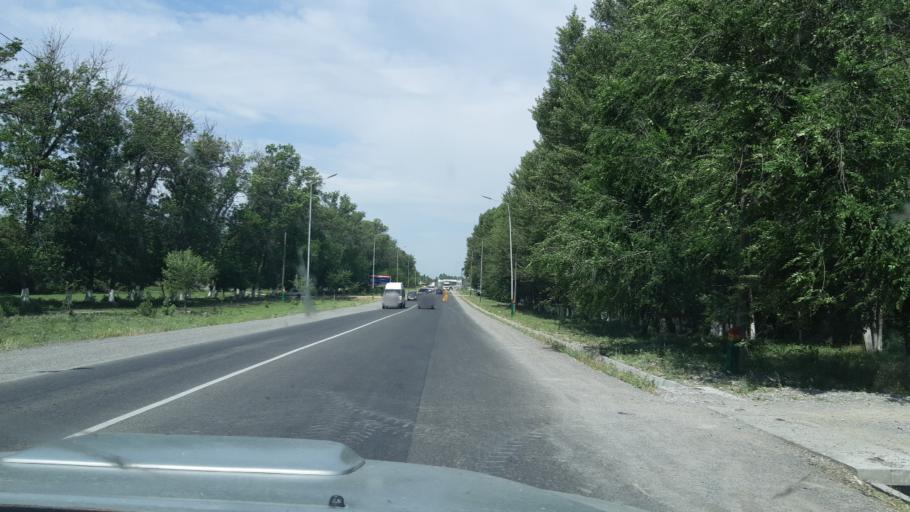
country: KZ
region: Ongtustik Qazaqstan
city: Turar Ryskulov
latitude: 42.5488
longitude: 70.3129
